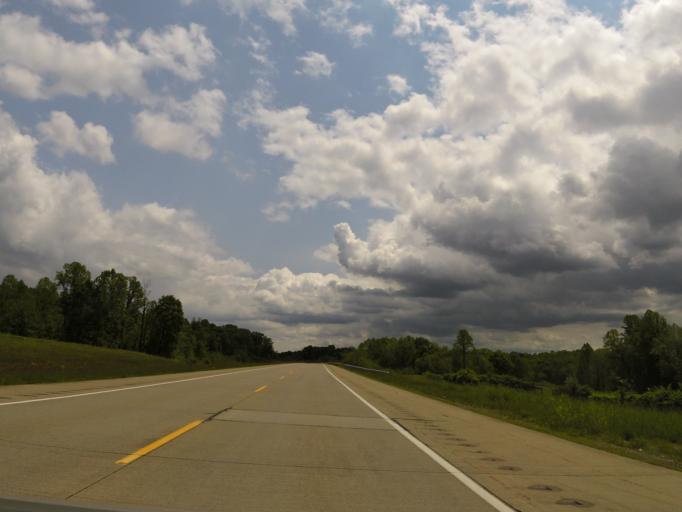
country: US
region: West Virginia
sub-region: Mason County
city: New Haven
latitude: 39.0073
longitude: -81.9023
